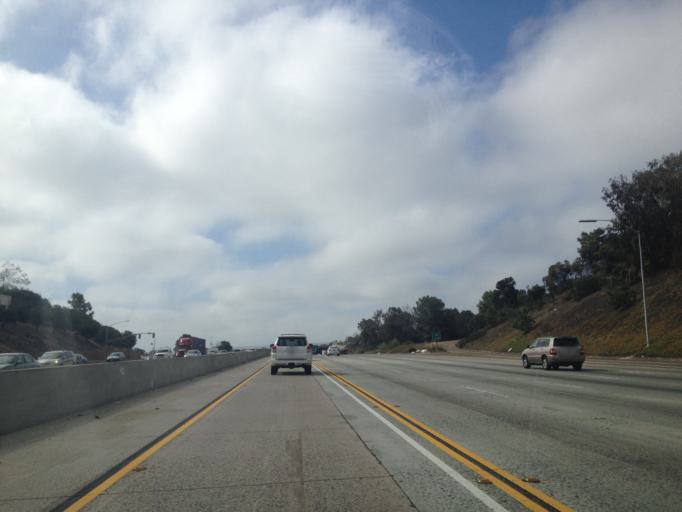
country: US
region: California
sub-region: San Diego County
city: Del Mar
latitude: 32.9540
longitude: -117.2445
